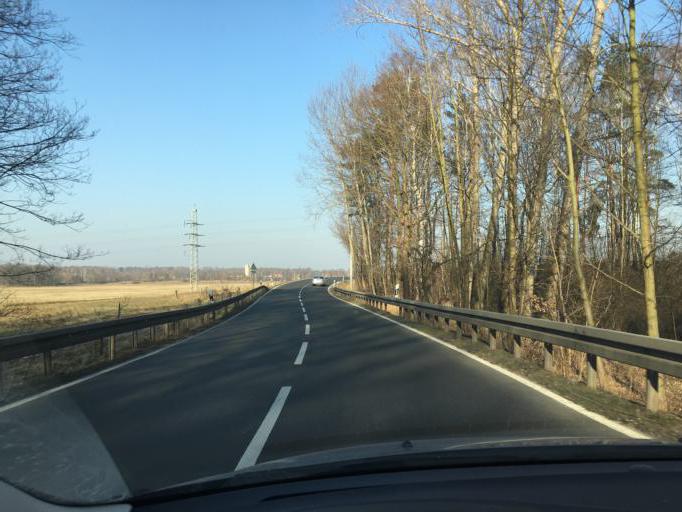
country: DE
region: Saxony
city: Bad Lausick
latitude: 51.1376
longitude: 12.6074
